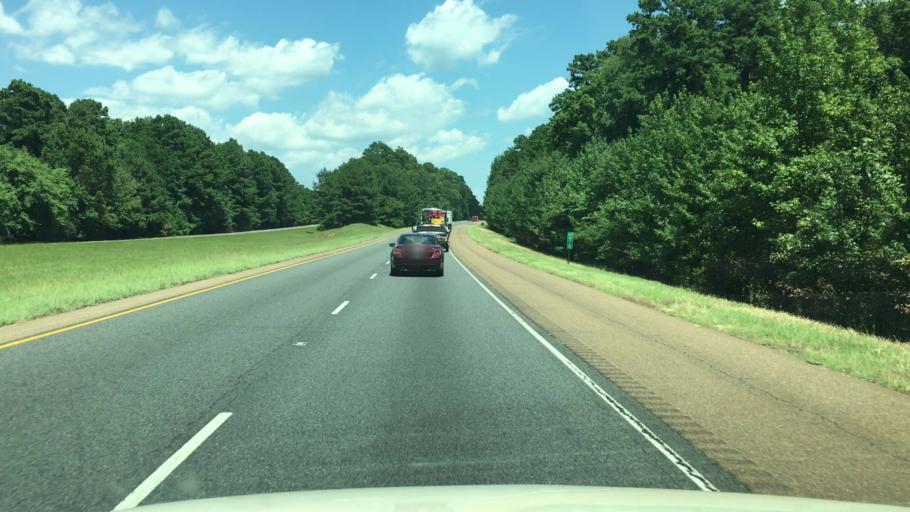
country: US
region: Arkansas
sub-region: Clark County
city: Gurdon
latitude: 33.9256
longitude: -93.2662
